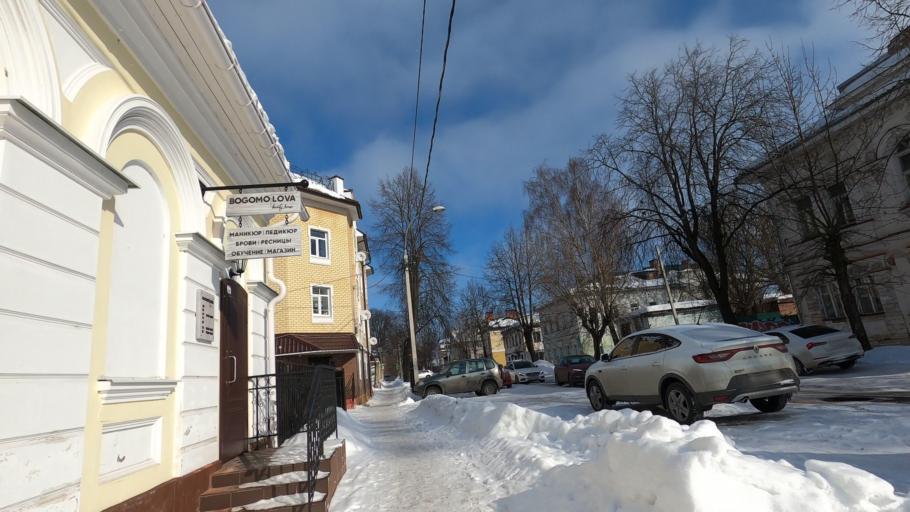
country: RU
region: Jaroslavl
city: Rybinsk
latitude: 58.0463
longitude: 38.8456
